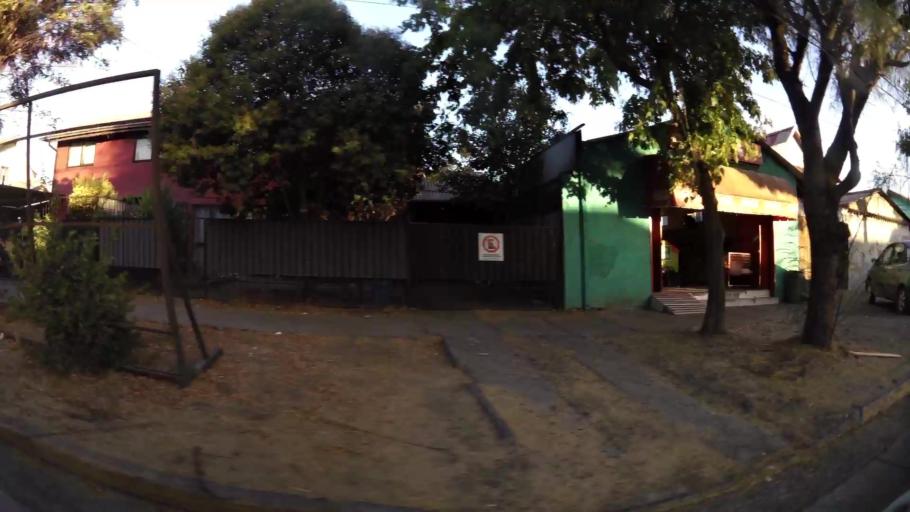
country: CL
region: Maule
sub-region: Provincia de Talca
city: Talca
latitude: -35.4415
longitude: -71.6782
